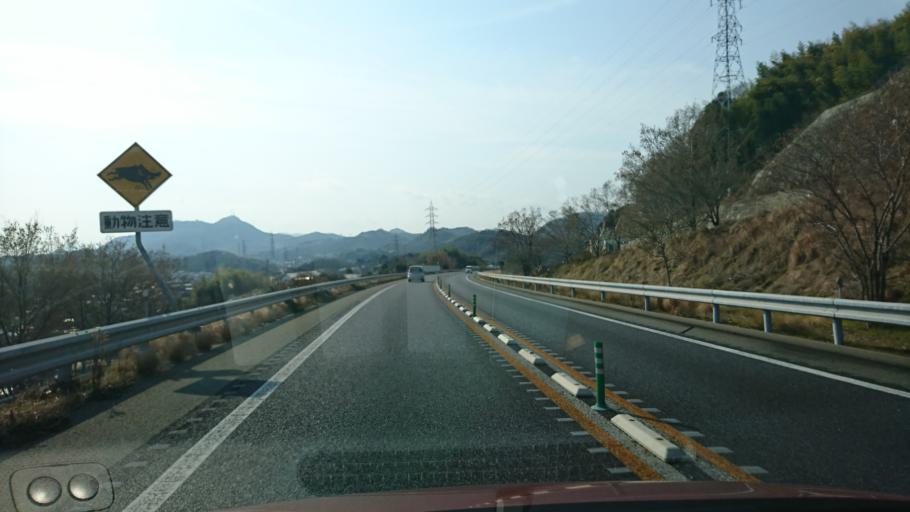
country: JP
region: Hiroshima
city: Onomichi
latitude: 34.4039
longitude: 133.2120
